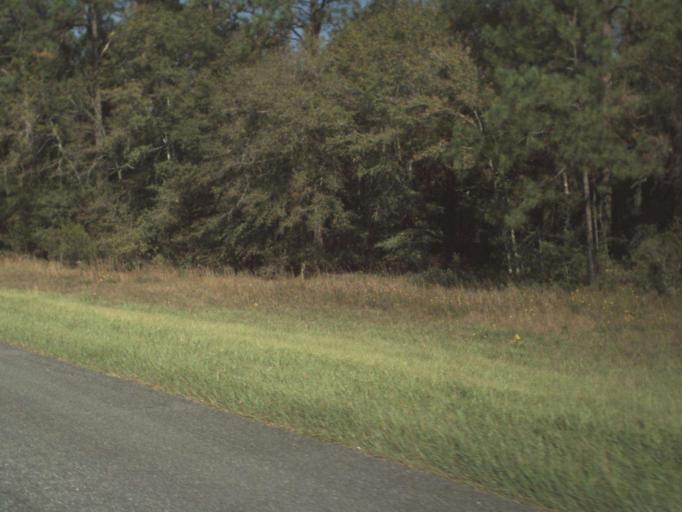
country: US
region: Florida
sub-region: Jackson County
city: Marianna
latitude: 30.7071
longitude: -85.1468
